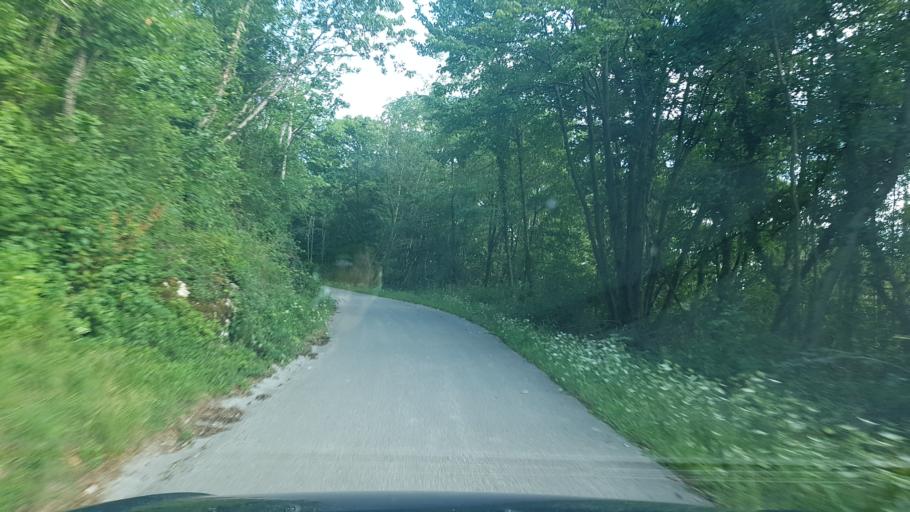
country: SI
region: Kanal
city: Deskle
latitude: 46.0295
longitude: 13.6065
